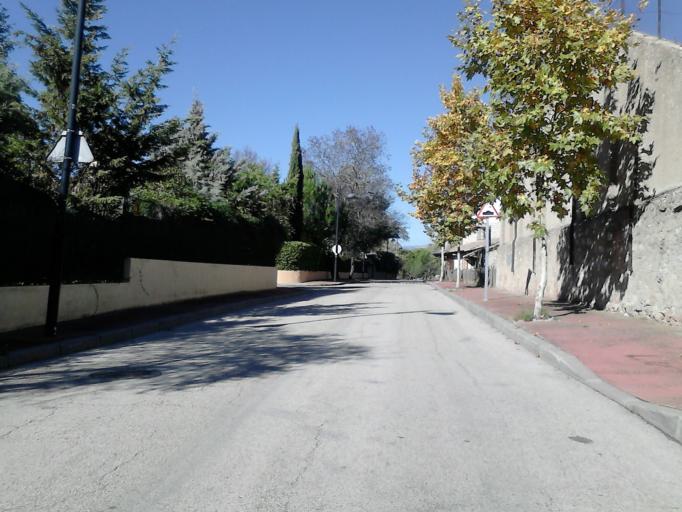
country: ES
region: Madrid
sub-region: Provincia de Madrid
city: Galapagar
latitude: 40.5684
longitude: -3.9918
